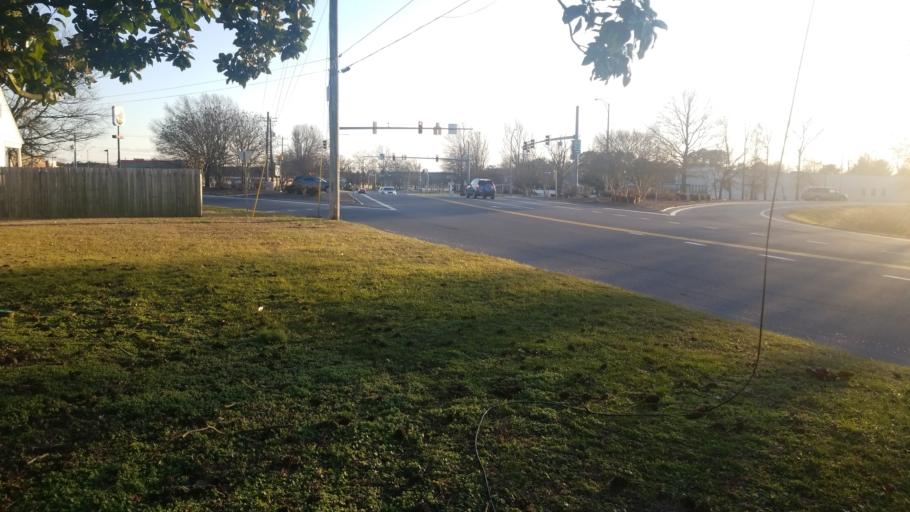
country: US
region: Maryland
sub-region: Wicomico County
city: Salisbury
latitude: 38.3699
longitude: -75.5730
